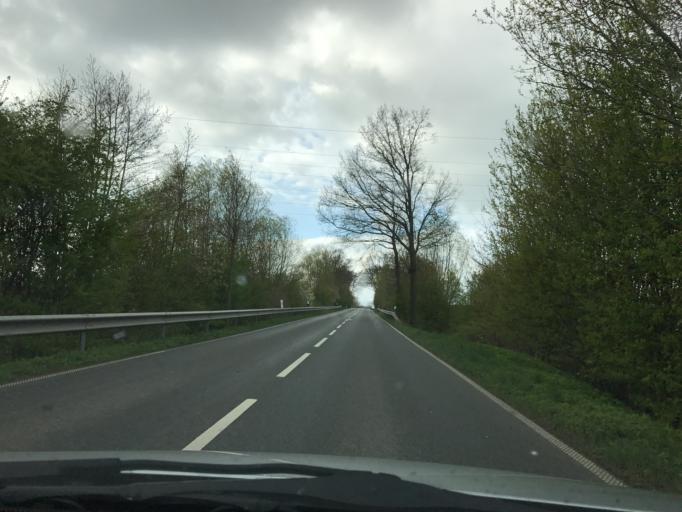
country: DE
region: Schleswig-Holstein
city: Altenkrempe
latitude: 54.1594
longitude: 10.8088
